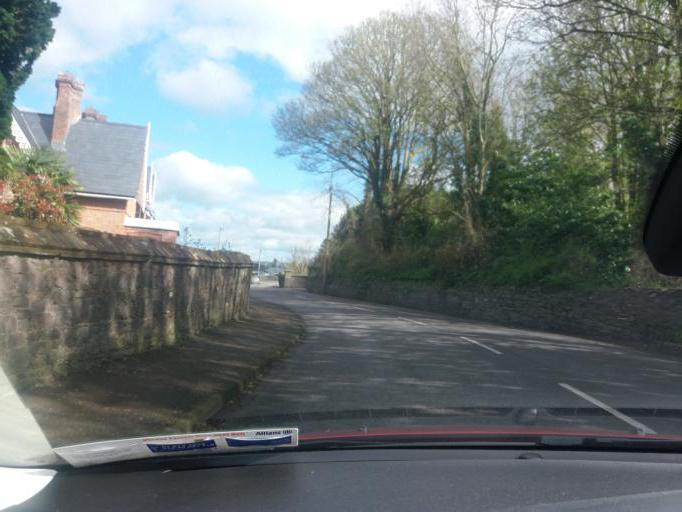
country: IE
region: Munster
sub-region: County Cork
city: Passage West
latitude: 51.8570
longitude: -8.3255
